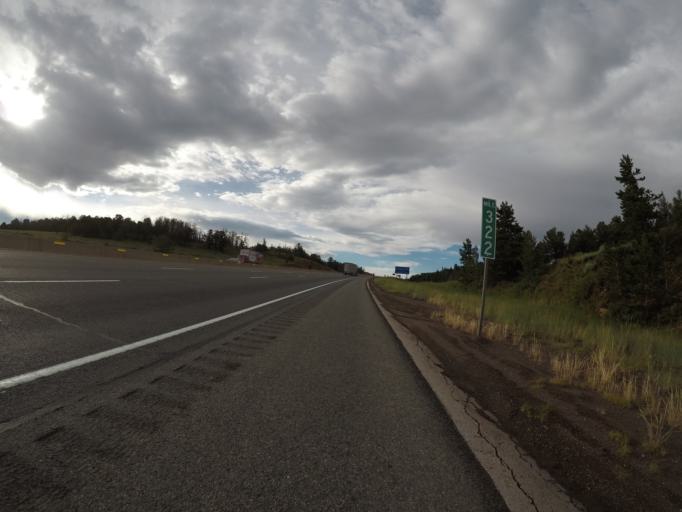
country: US
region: Wyoming
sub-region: Albany County
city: Laramie
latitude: 41.2537
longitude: -105.4468
